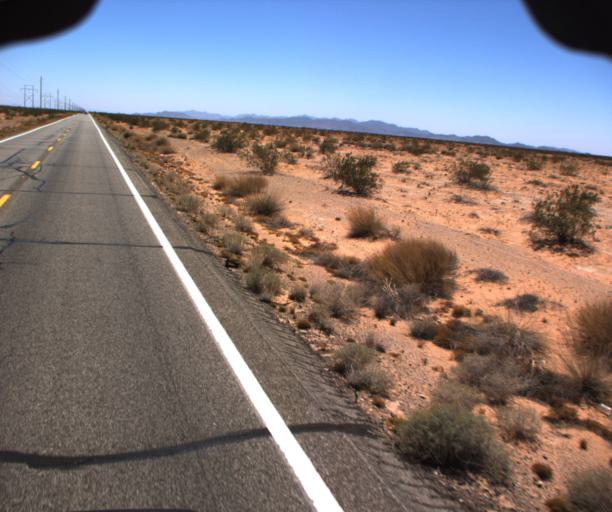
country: US
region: Arizona
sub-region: La Paz County
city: Quartzsite
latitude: 33.8832
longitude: -114.2170
